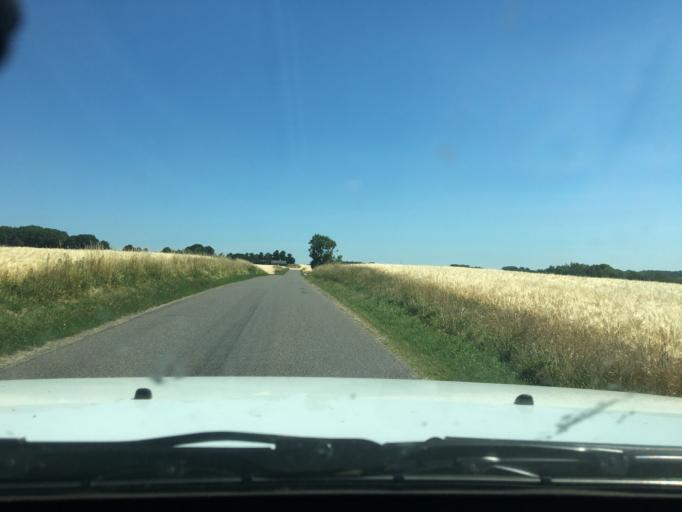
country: DK
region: Central Jutland
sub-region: Horsens Kommune
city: Braedstrup
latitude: 55.9375
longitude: 9.5448
